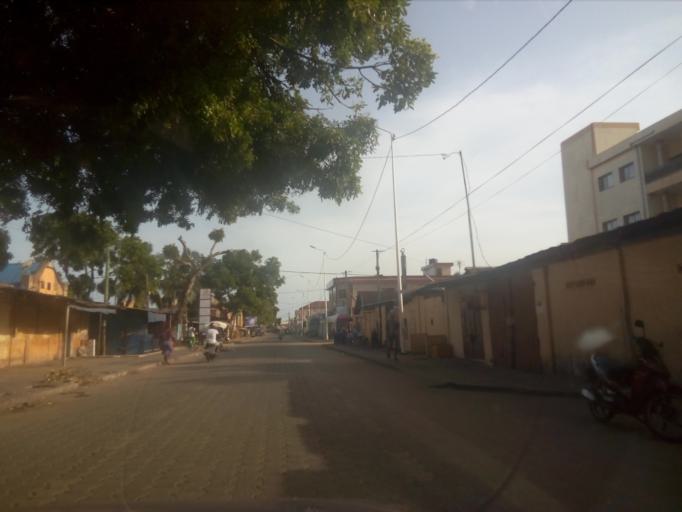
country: TG
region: Maritime
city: Lome
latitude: 6.1339
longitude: 1.2275
